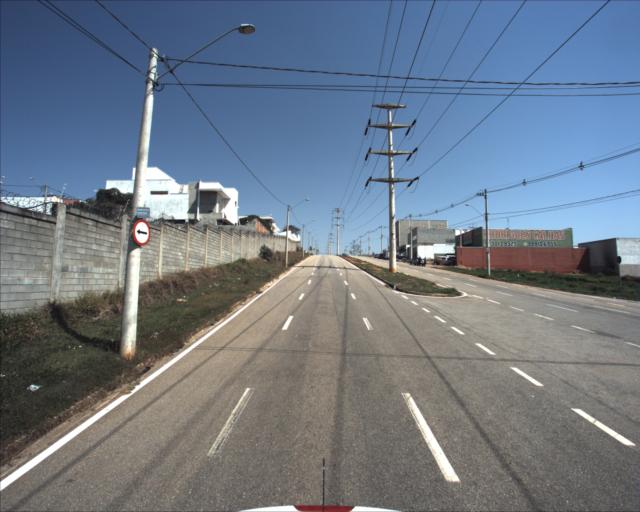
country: BR
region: Sao Paulo
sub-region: Sorocaba
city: Sorocaba
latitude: -23.4462
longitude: -47.5109
